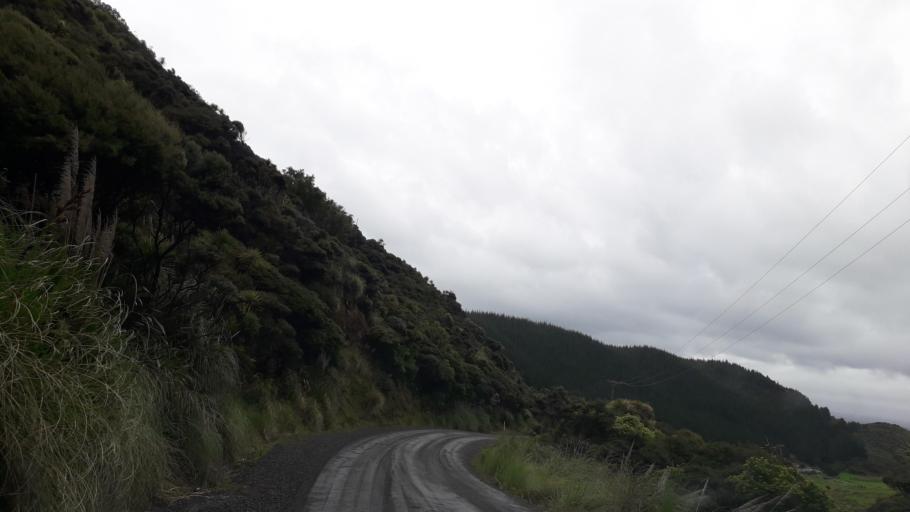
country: NZ
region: Northland
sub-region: Far North District
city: Ahipara
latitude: -35.4378
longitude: 173.3049
